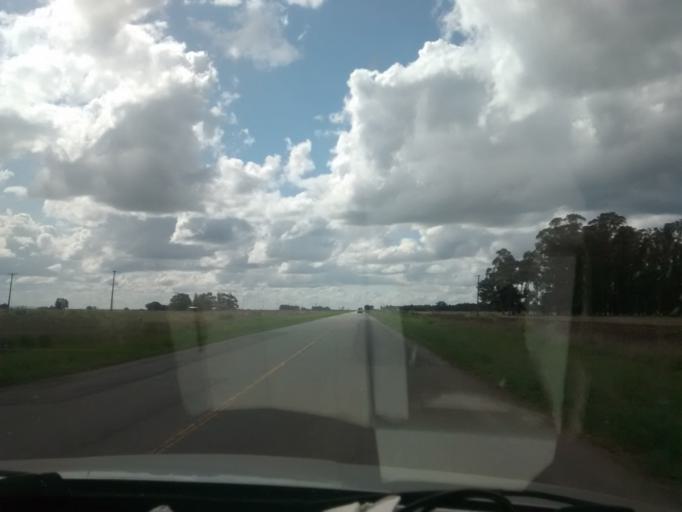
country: AR
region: Buenos Aires
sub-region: Partido de Loberia
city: Loberia
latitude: -37.7091
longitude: -58.7233
